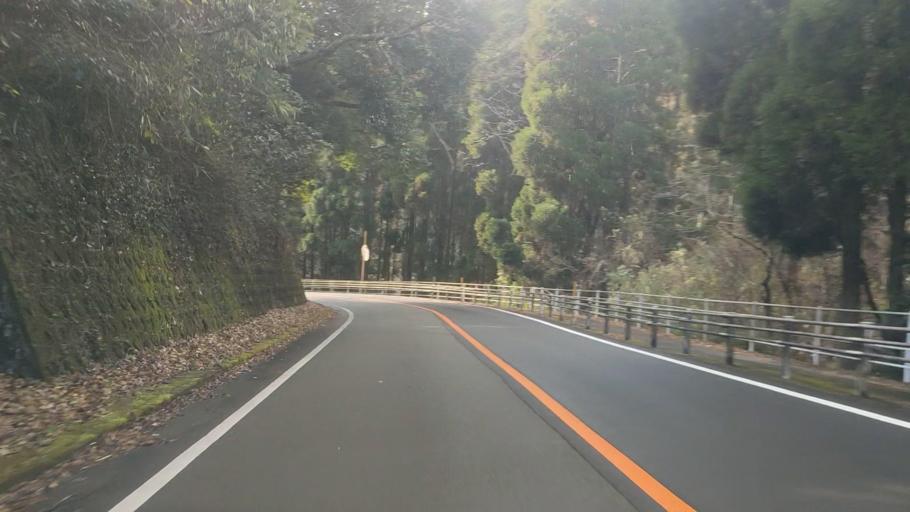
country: JP
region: Kumamoto
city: Hitoyoshi
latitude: 32.2920
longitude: 130.8422
